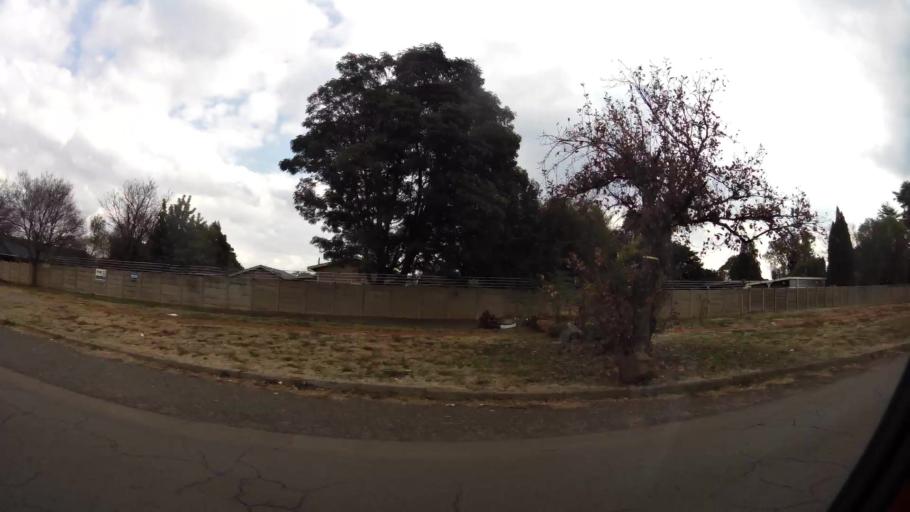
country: ZA
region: Gauteng
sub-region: Sedibeng District Municipality
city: Vanderbijlpark
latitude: -26.7261
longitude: 27.8371
